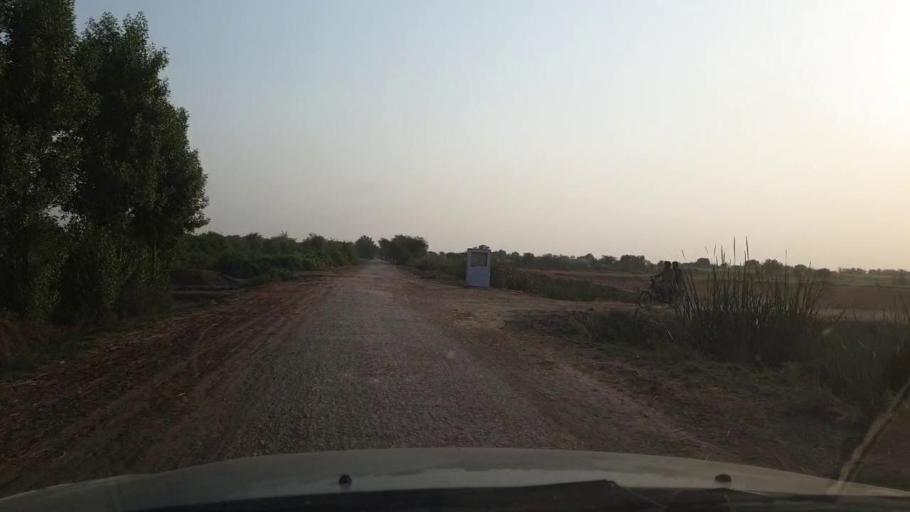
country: PK
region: Sindh
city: Tando Muhammad Khan
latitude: 25.0142
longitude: 68.4381
